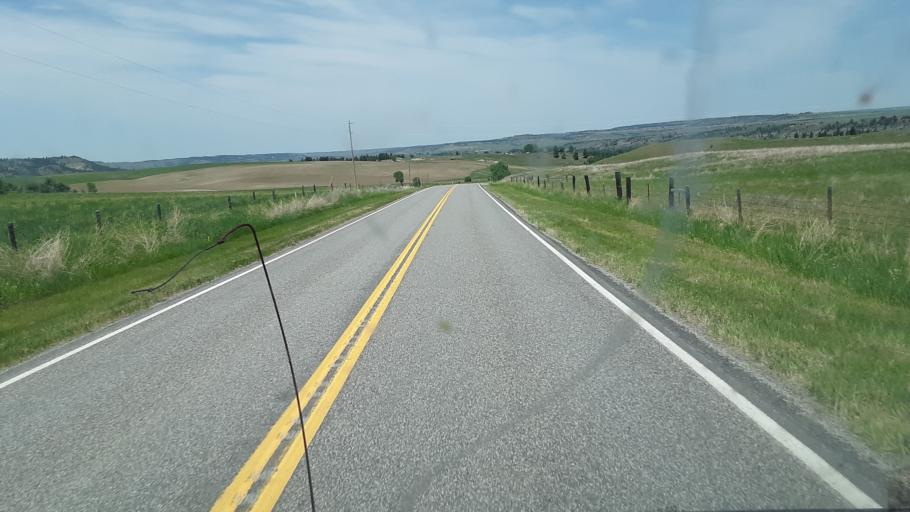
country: US
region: Montana
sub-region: Stillwater County
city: Columbus
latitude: 45.5936
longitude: -109.1956
